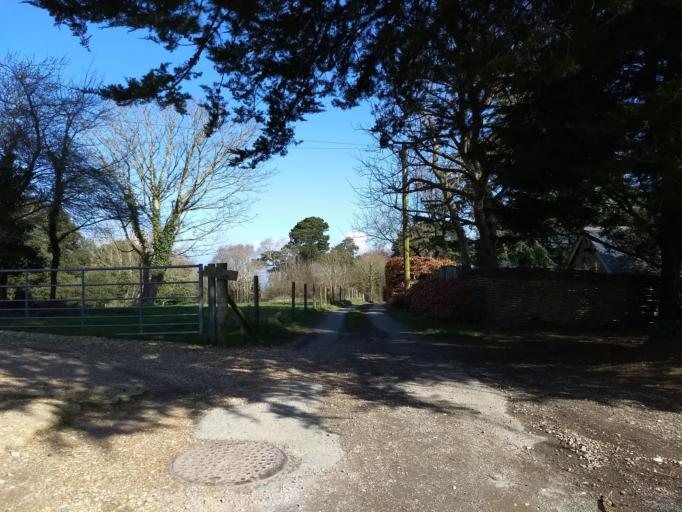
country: GB
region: England
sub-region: Isle of Wight
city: Seaview
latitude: 50.7104
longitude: -1.1075
